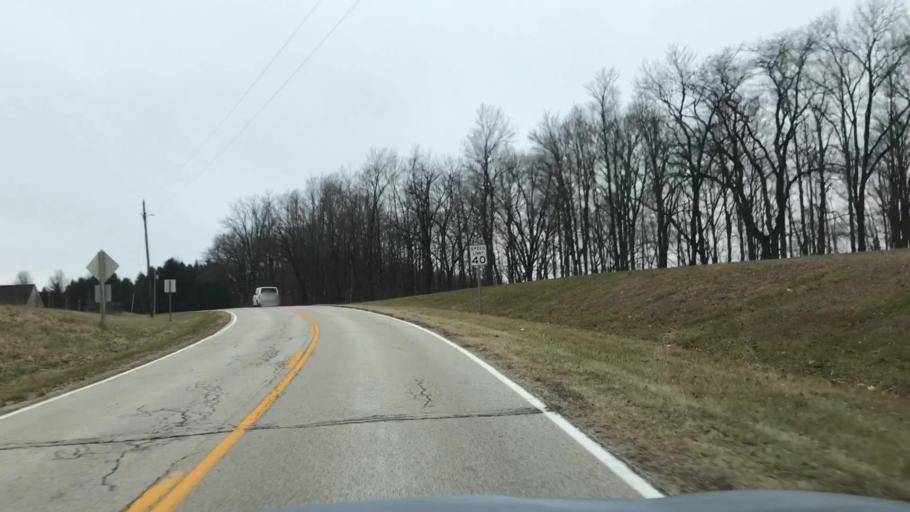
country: US
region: Illinois
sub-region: McLean County
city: Hudson
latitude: 40.6267
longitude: -88.9264
